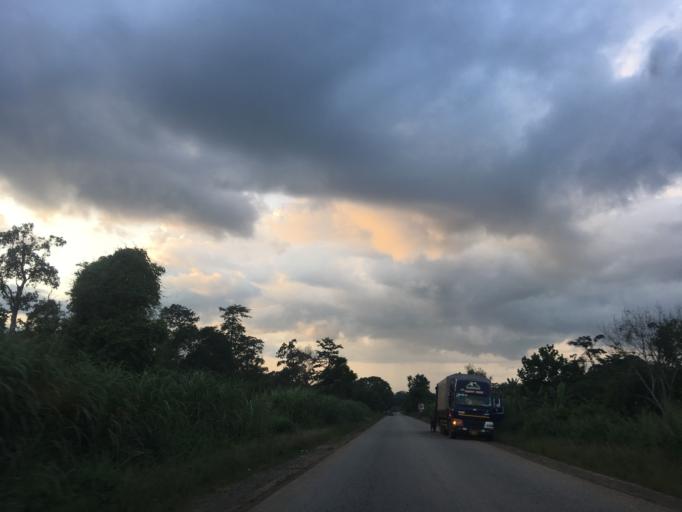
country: GH
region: Western
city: Bibiani
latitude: 6.7450
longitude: -2.5039
